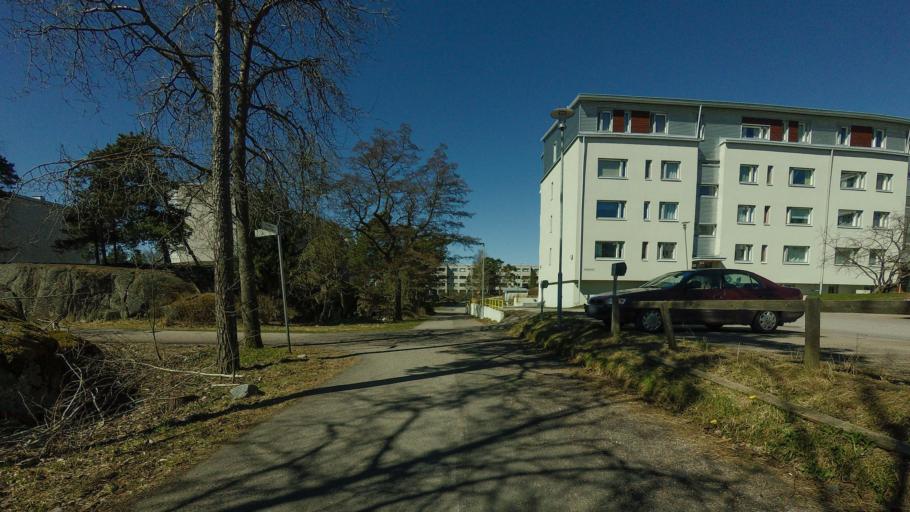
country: FI
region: Uusimaa
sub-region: Helsinki
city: Helsinki
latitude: 60.1692
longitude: 25.0389
